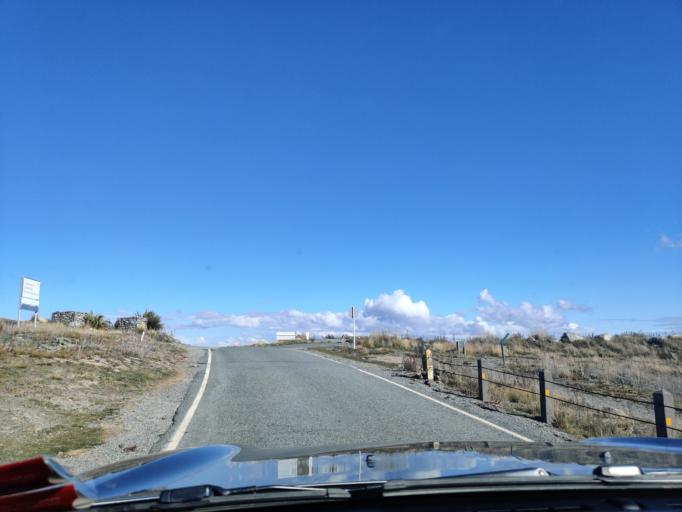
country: NZ
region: Canterbury
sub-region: Timaru District
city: Pleasant Point
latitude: -43.9855
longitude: 170.4638
